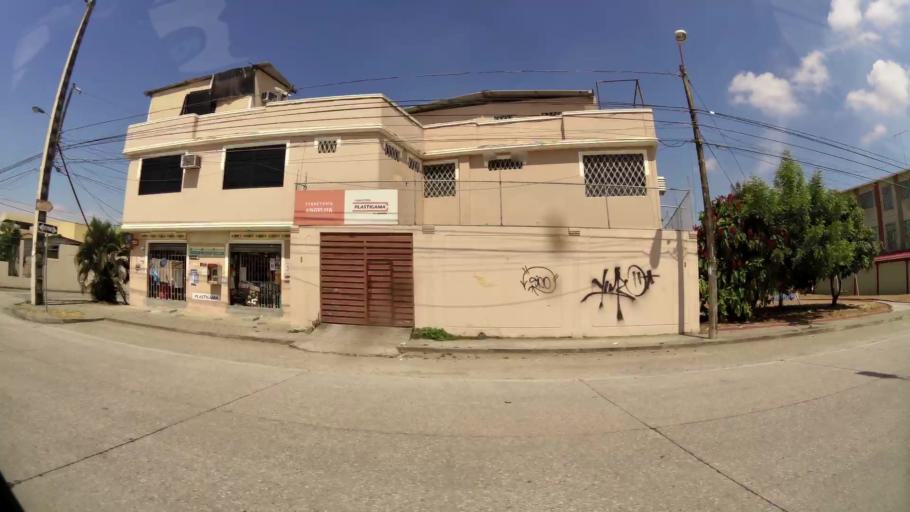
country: EC
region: Guayas
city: Eloy Alfaro
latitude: -2.1079
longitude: -79.9026
